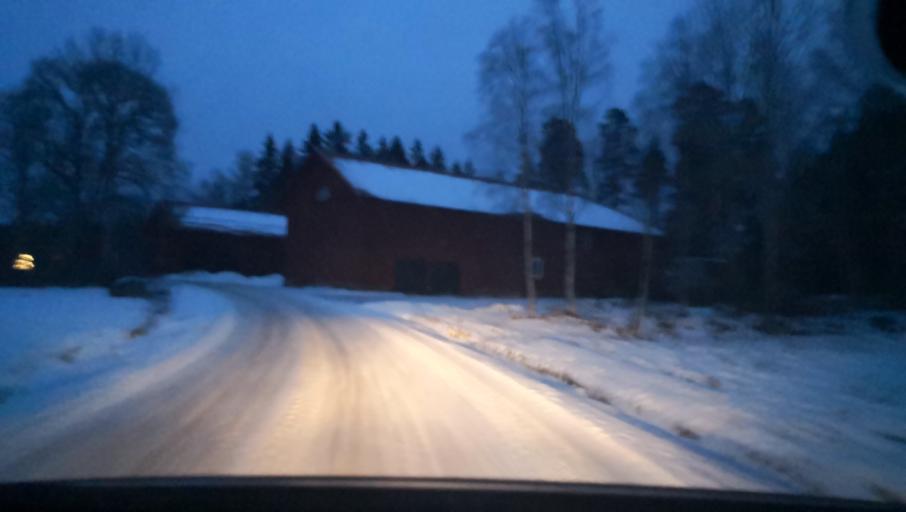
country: SE
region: Uppsala
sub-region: Heby Kommun
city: Tarnsjo
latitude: 60.2421
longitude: 16.6966
